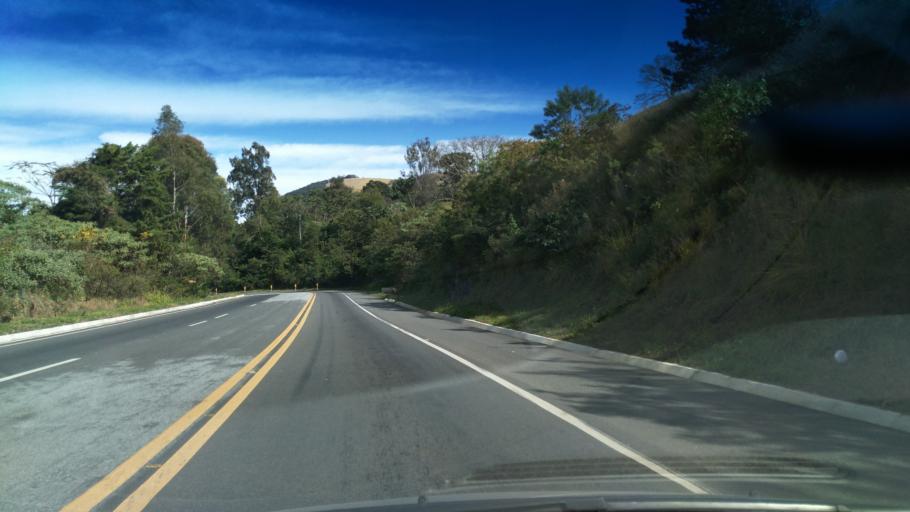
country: BR
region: Minas Gerais
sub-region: Borda Da Mata
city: Borda da Mata
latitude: -22.1316
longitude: -46.1763
